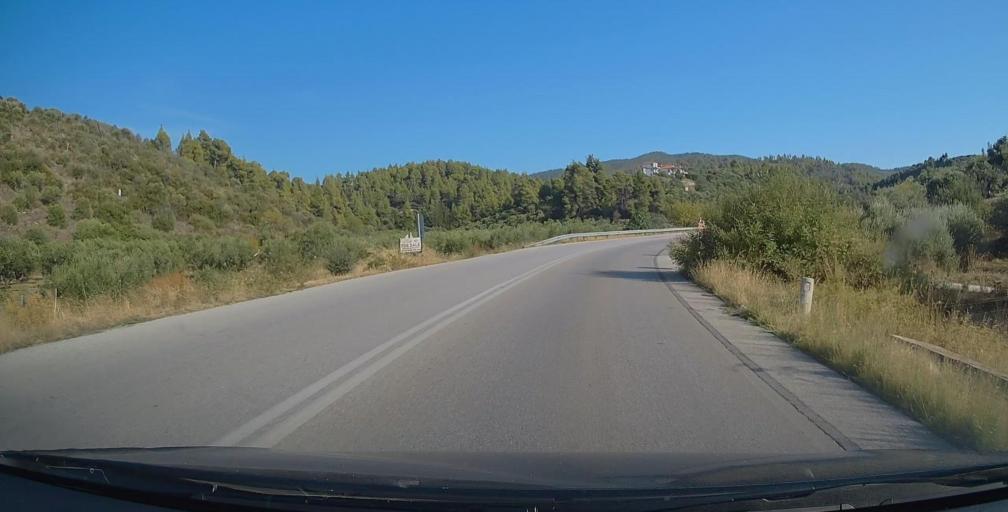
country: GR
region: Central Macedonia
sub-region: Nomos Chalkidikis
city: Neos Marmaras
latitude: 40.0849
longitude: 23.8081
